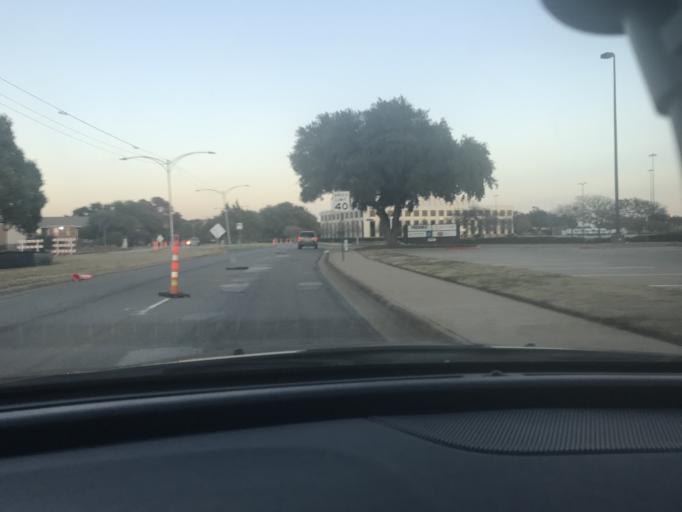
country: US
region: Texas
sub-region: Tarrant County
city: Arlington
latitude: 32.7625
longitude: -97.1064
